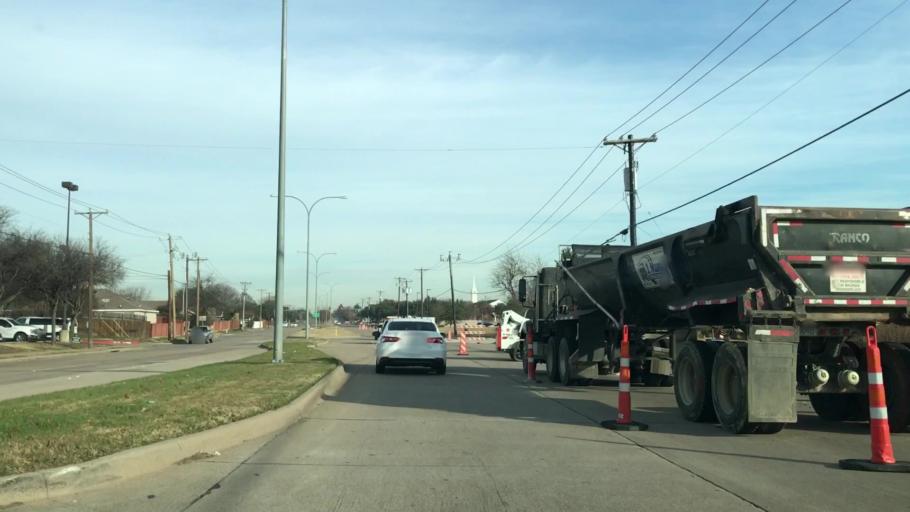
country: US
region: Texas
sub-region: Tarrant County
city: Watauga
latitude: 32.8743
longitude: -97.2897
